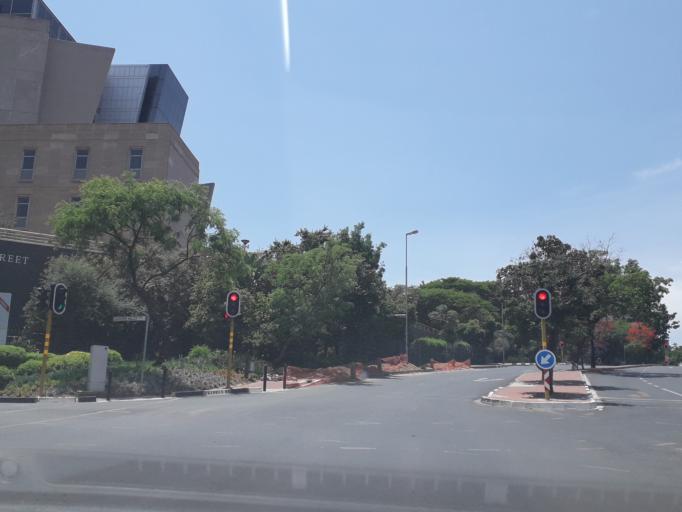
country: ZA
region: Gauteng
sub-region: City of Johannesburg Metropolitan Municipality
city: Johannesburg
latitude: -26.1038
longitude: 28.0512
